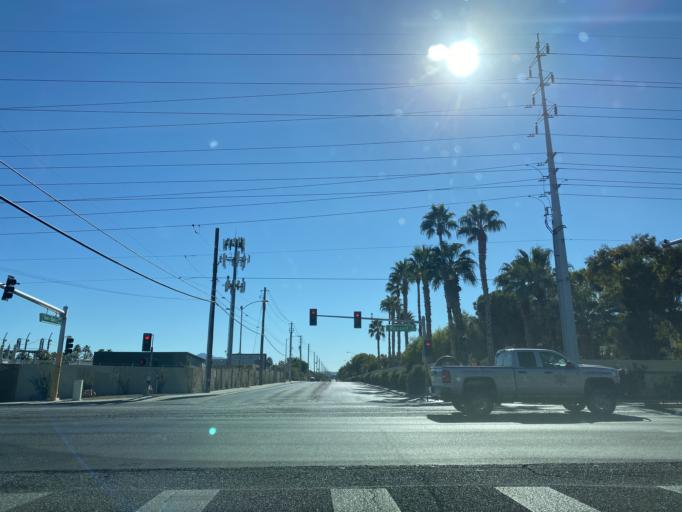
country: US
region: Nevada
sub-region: Clark County
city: Whitney
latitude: 36.0858
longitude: -115.0868
